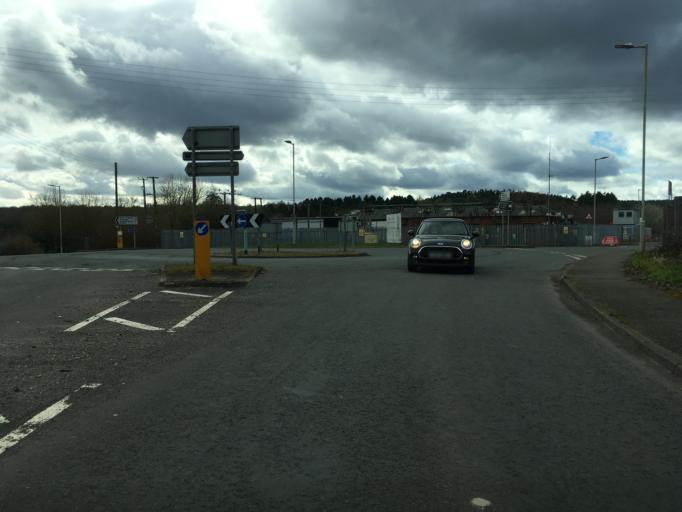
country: GB
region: England
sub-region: Gloucestershire
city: Cinderford
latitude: 51.8227
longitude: -2.5093
